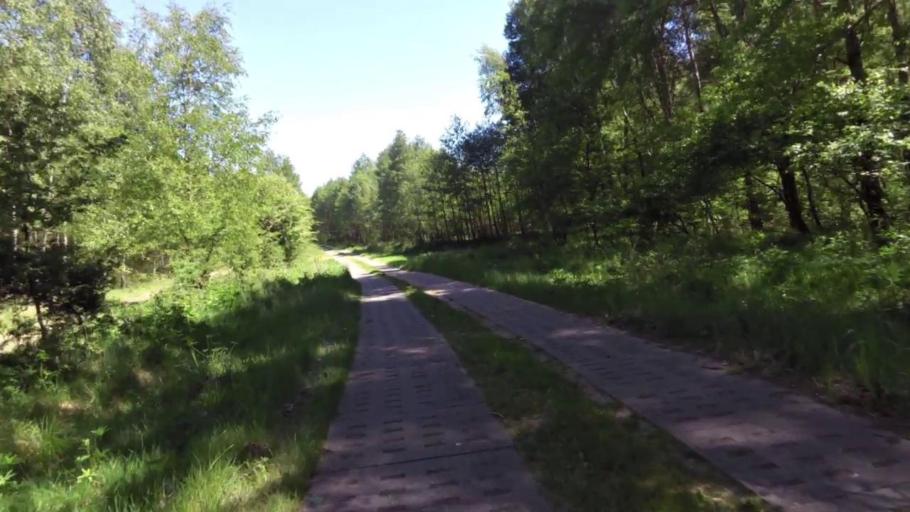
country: PL
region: West Pomeranian Voivodeship
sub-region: Powiat szczecinecki
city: Borne Sulinowo
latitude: 53.5666
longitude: 16.6242
